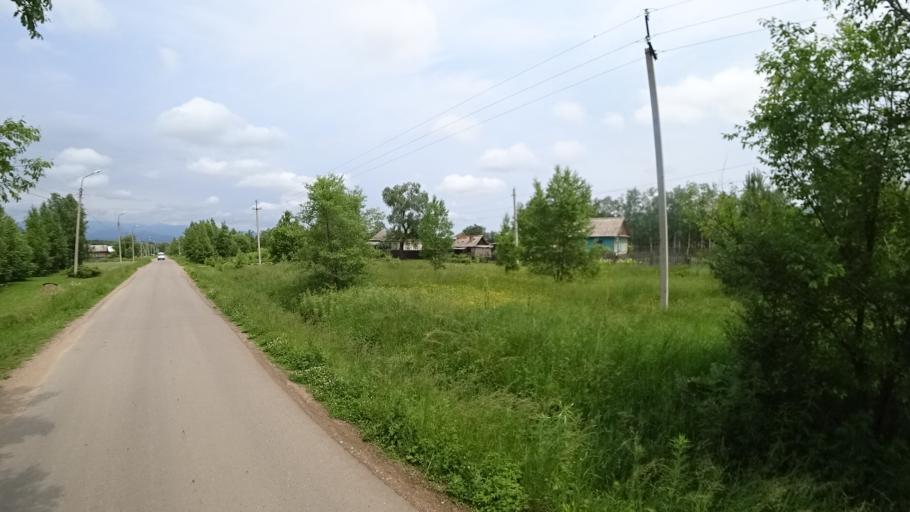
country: RU
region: Primorskiy
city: Novosysoyevka
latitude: 44.2339
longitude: 133.3595
